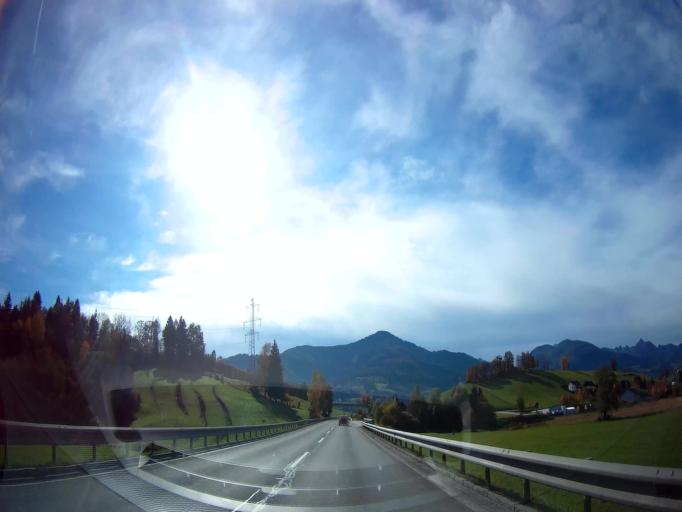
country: AT
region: Styria
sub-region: Politischer Bezirk Liezen
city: Grobming
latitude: 47.4486
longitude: 13.9126
